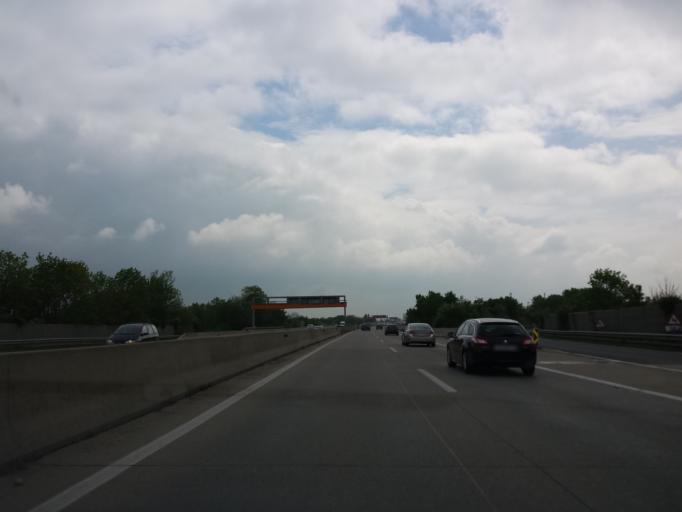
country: AT
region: Lower Austria
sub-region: Politischer Bezirk Wien-Umgebung
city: Schwechat
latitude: 48.1519
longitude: 16.4848
